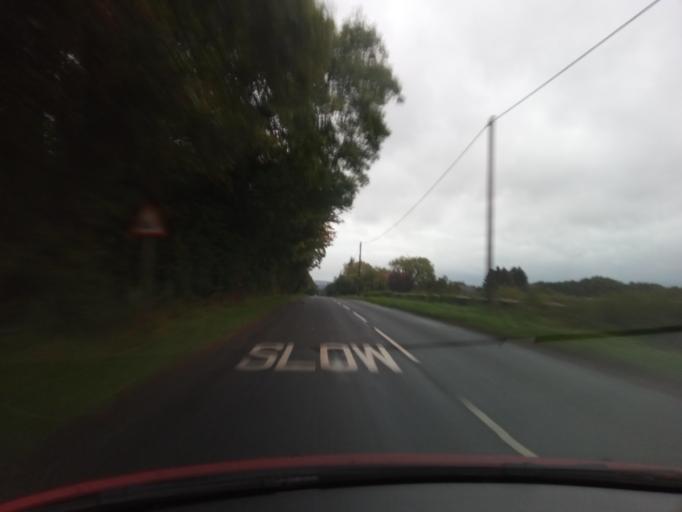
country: GB
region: England
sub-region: Darlington
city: High Coniscliffe
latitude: 54.5247
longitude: -1.6720
